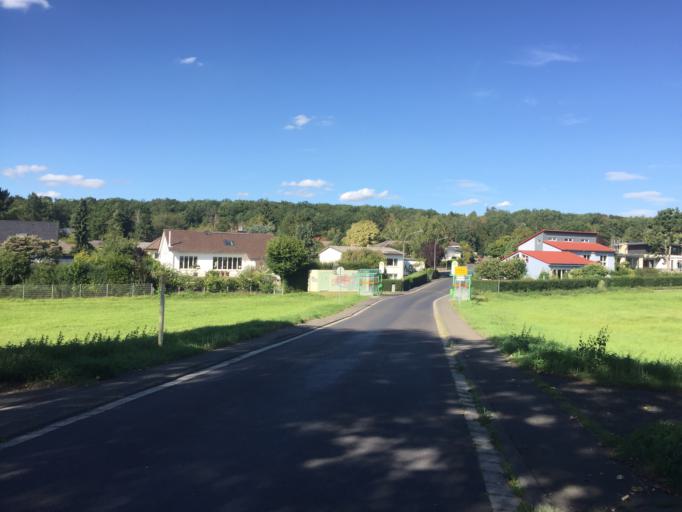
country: DE
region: Hesse
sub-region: Regierungsbezirk Giessen
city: Langgons
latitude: 50.5355
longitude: 8.6834
